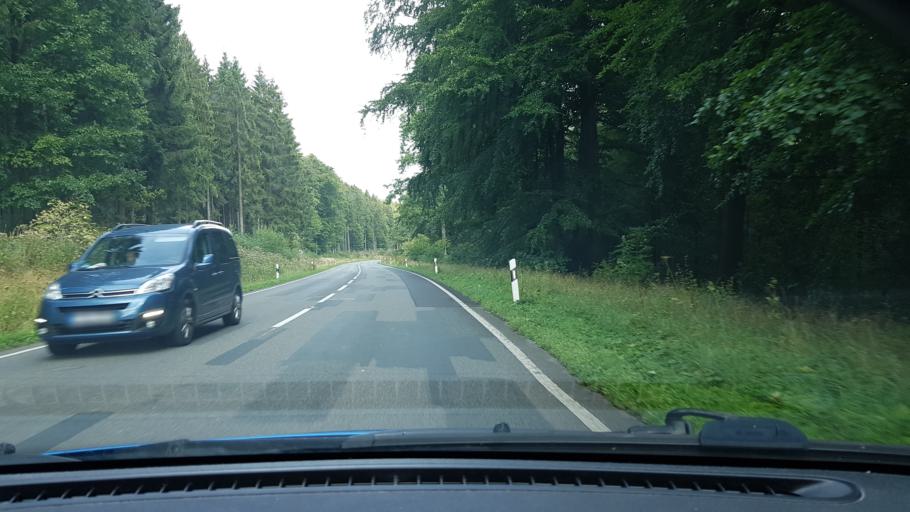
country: DE
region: Lower Saxony
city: Egestorf
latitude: 52.2697
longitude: 9.4863
